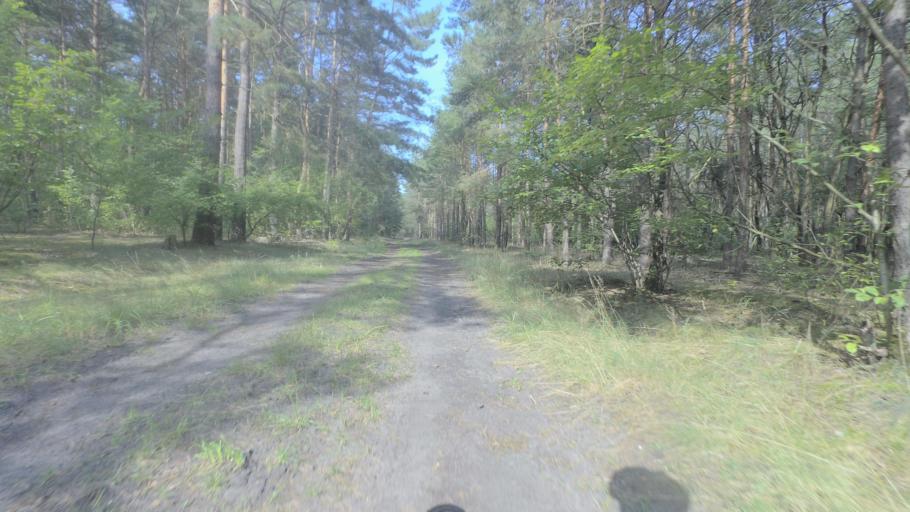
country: DE
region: Brandenburg
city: Rangsdorf
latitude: 52.2525
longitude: 13.4033
